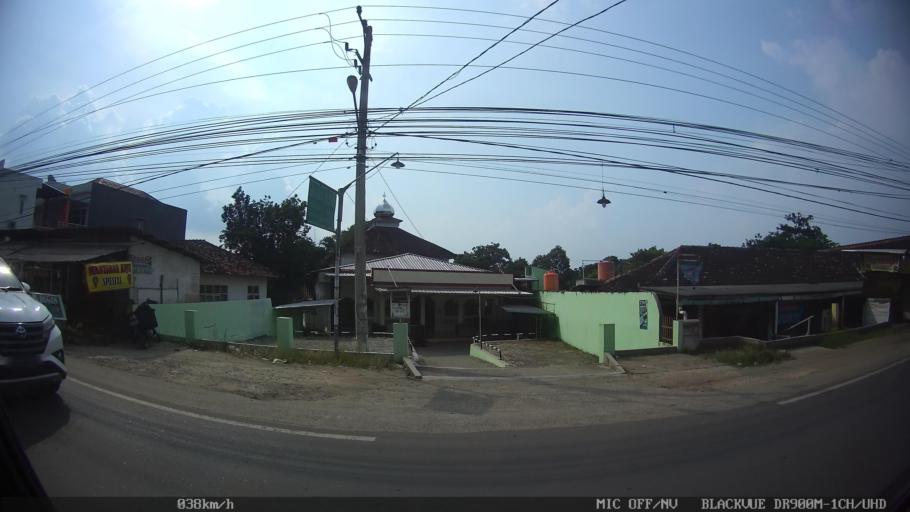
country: ID
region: Lampung
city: Kedaton
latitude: -5.3623
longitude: 105.2238
